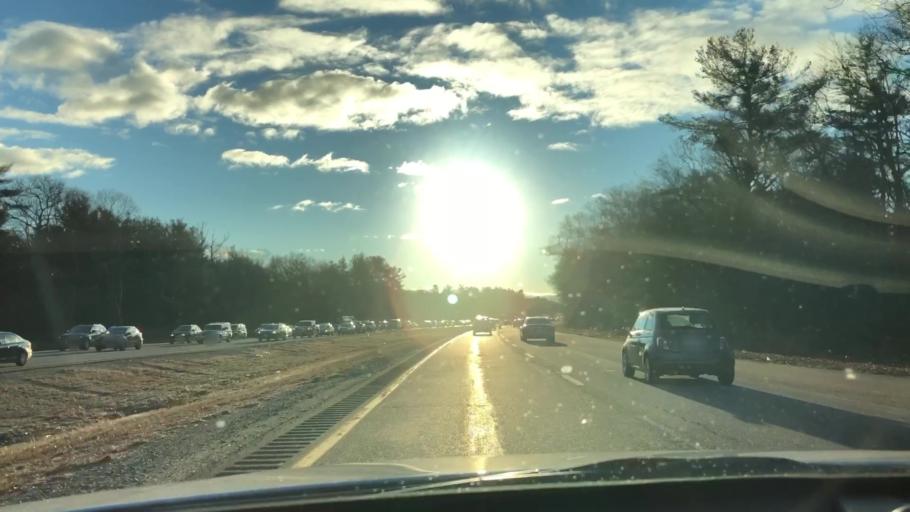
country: US
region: Massachusetts
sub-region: Norfolk County
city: Weymouth
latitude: 42.1819
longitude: -70.9205
